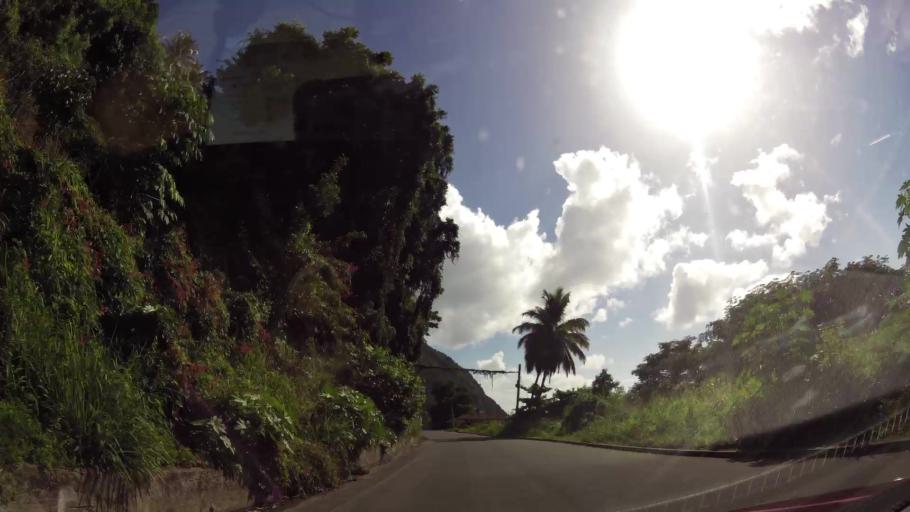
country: DM
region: Saint Luke
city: Pointe Michel
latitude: 15.2810
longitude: -61.3746
